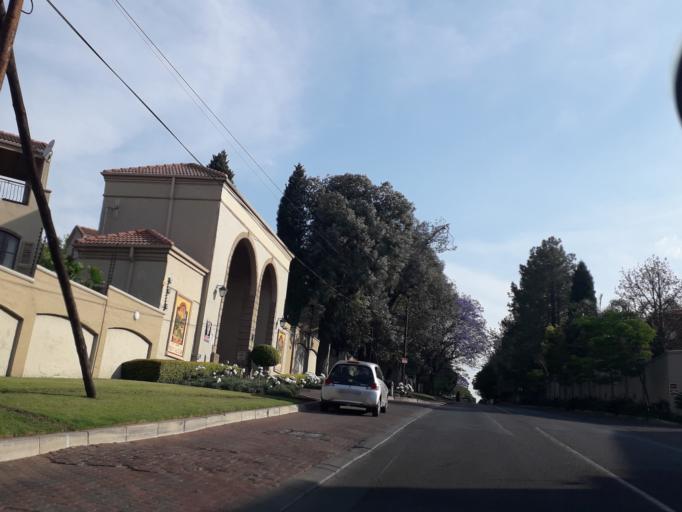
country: ZA
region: Gauteng
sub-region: City of Johannesburg Metropolitan Municipality
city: Johannesburg
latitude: -26.0901
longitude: 28.0407
